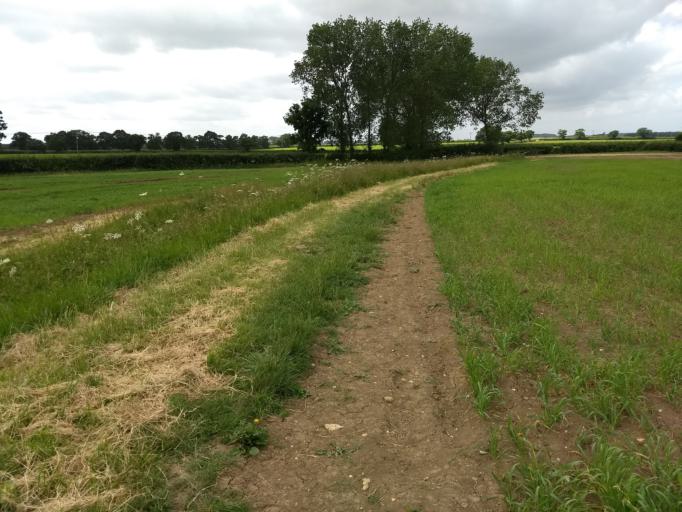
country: GB
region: England
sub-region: Milton Keynes
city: Calverton
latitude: 52.0155
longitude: -0.8258
